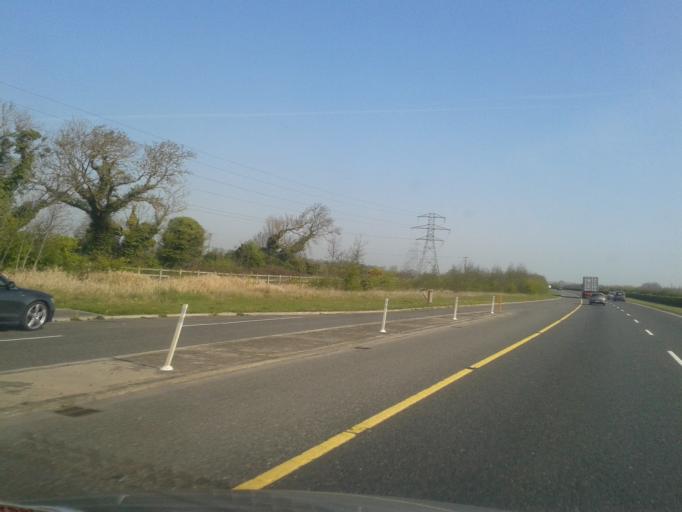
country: IE
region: Leinster
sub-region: Fingal County
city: Swords
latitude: 53.4956
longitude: -6.2013
